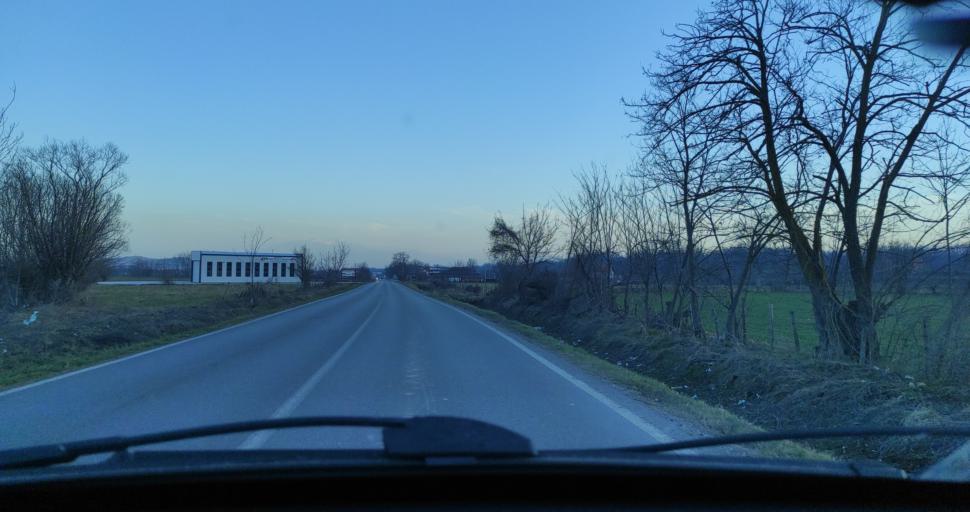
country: XK
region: Gjakova
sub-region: Komuna e Decanit
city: Dranoc
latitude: 42.5163
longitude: 20.3064
